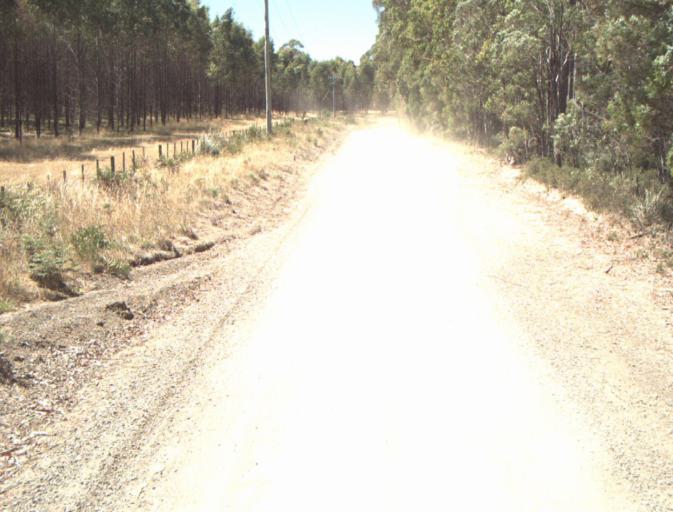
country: AU
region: Tasmania
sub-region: Launceston
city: Newstead
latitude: -41.3423
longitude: 147.3509
